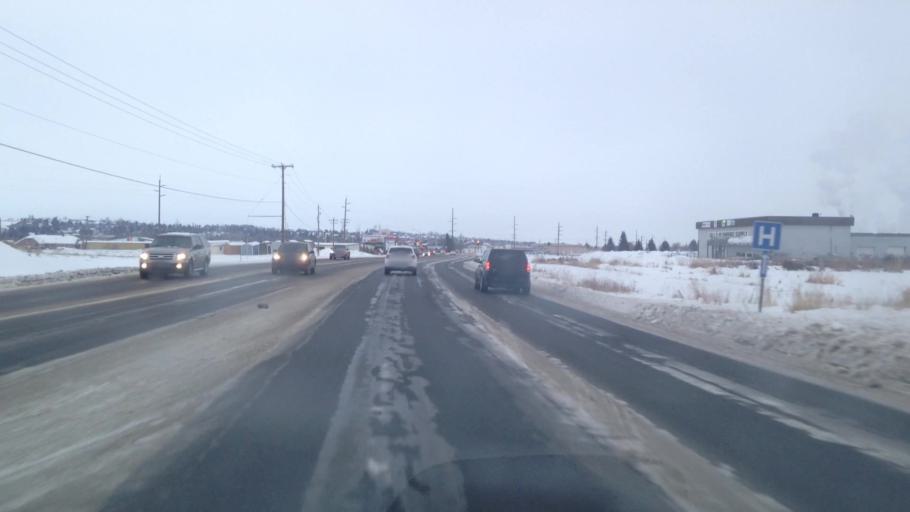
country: US
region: Idaho
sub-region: Madison County
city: Rexburg
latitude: 43.8458
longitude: -111.7780
